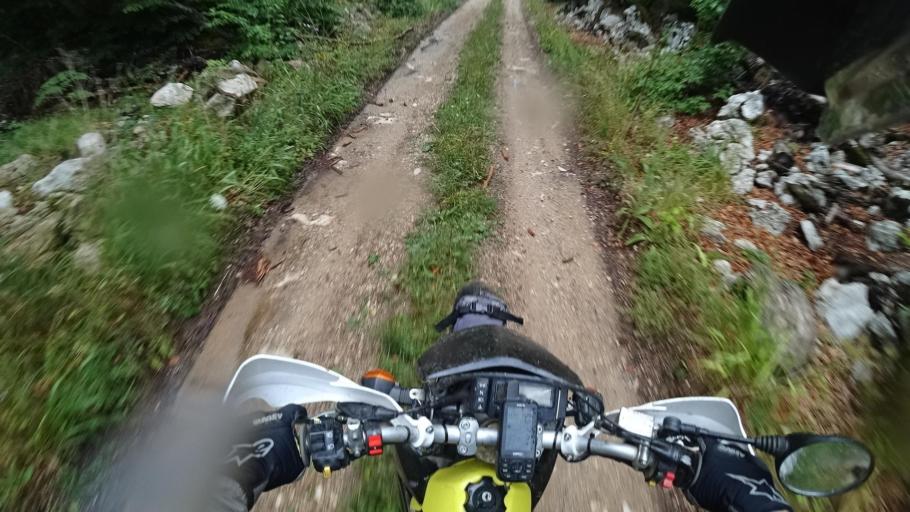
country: HR
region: Licko-Senjska
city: Jezerce
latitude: 44.7265
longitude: 15.6489
